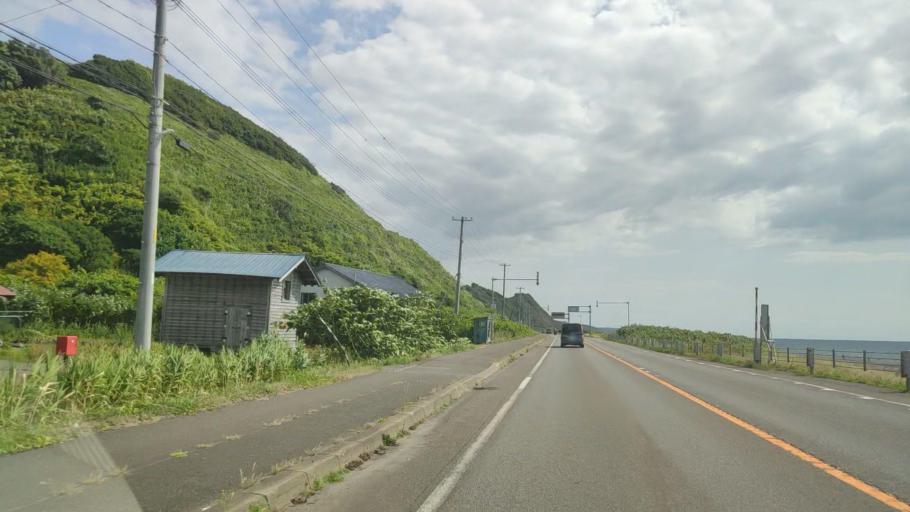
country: JP
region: Hokkaido
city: Rumoi
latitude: 44.2213
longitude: 141.6551
